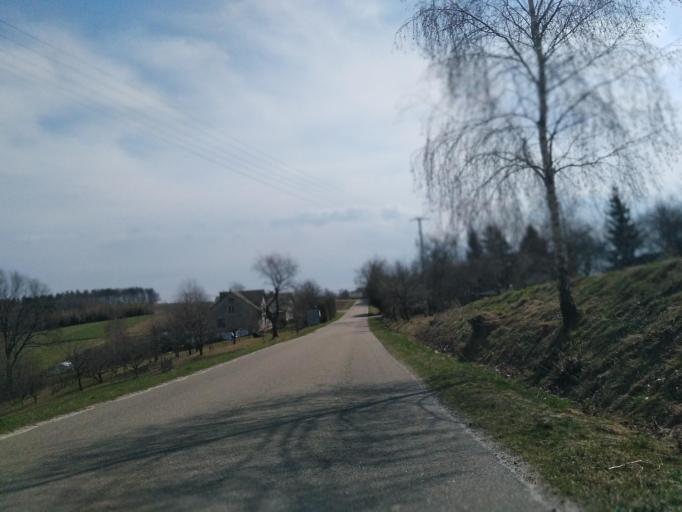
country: PL
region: Subcarpathian Voivodeship
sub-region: Powiat ropczycko-sedziszowski
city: Iwierzyce
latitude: 49.9775
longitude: 21.7458
